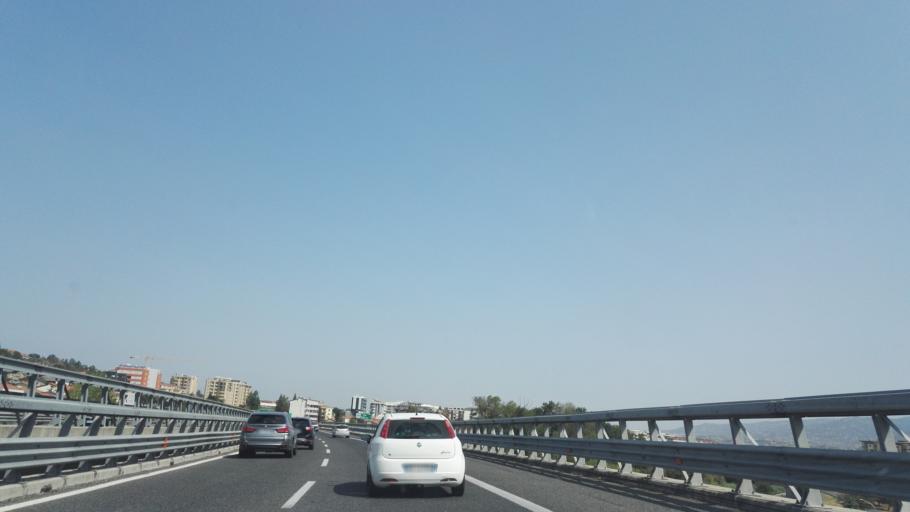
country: IT
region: Calabria
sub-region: Provincia di Cosenza
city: Cosenza
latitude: 39.3175
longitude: 16.2415
